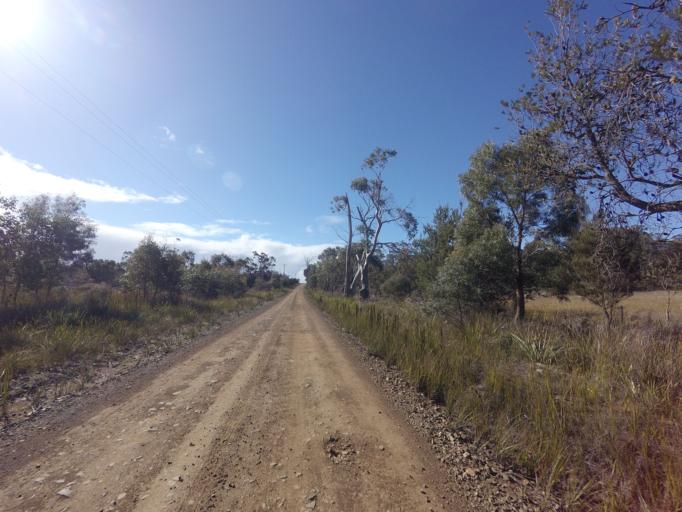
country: AU
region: Tasmania
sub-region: Sorell
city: Sorell
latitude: -42.3501
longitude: 147.9721
